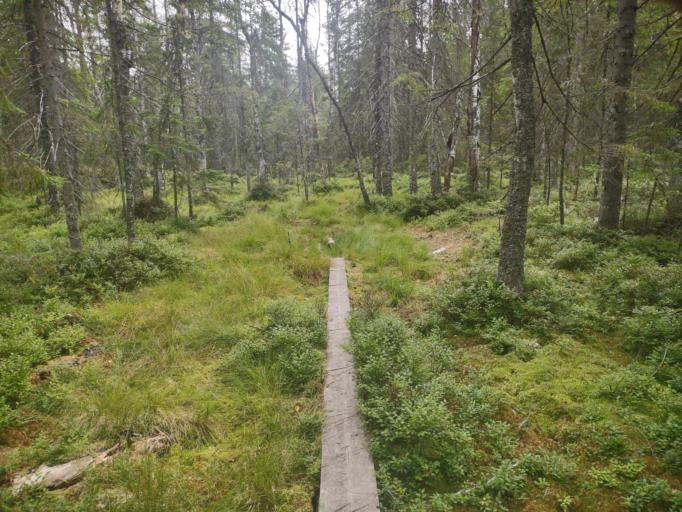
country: NO
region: Akershus
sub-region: Enebakk
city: Flateby
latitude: 59.8167
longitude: 11.0975
